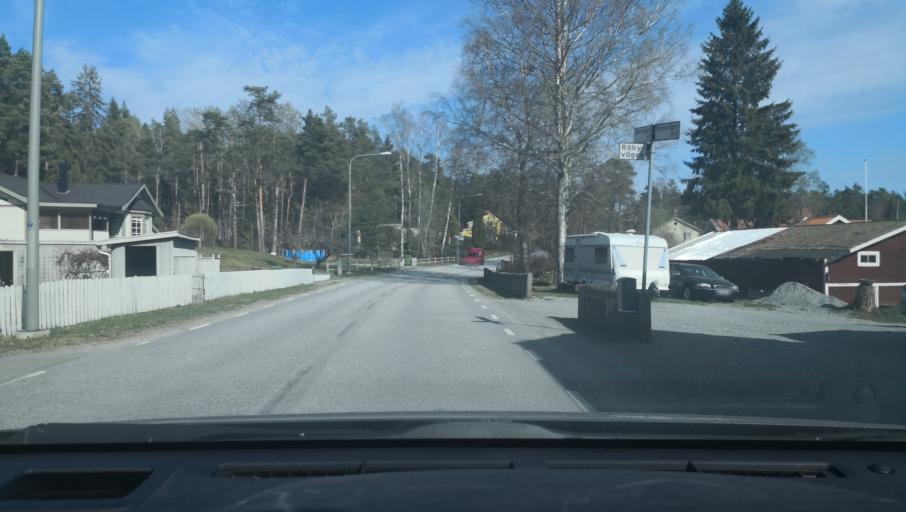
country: SE
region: Uppsala
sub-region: Enkopings Kommun
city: Irsta
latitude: 59.7773
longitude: 16.9316
